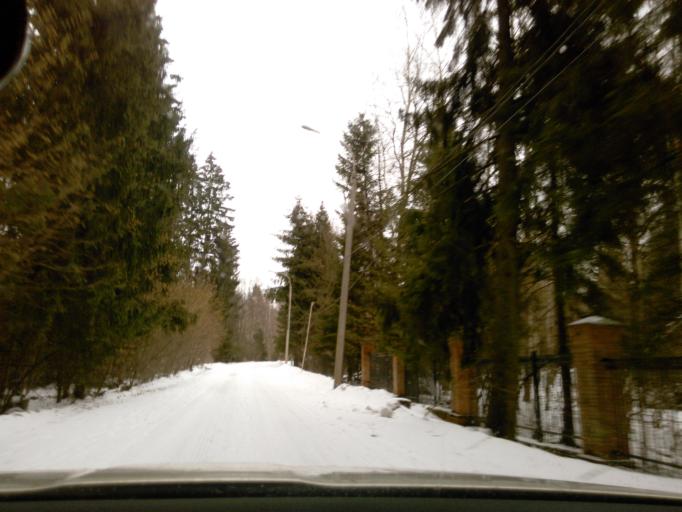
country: RU
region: Moskovskaya
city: Skhodnya
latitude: 55.9700
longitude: 37.2760
